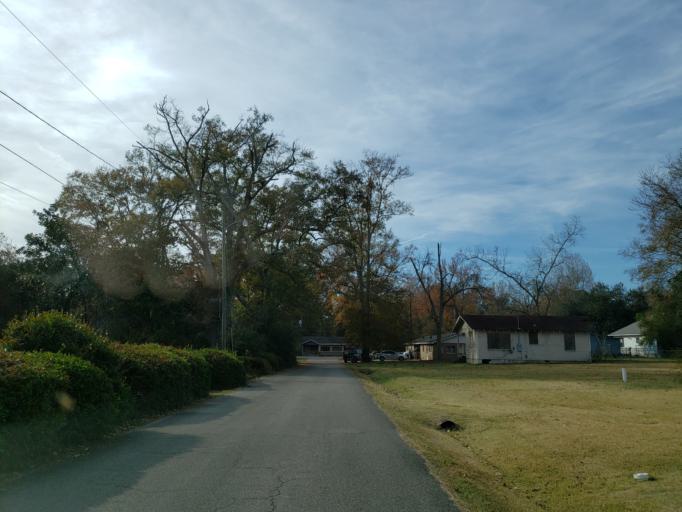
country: US
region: Mississippi
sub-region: Forrest County
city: Hattiesburg
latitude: 31.3342
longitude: -89.3124
